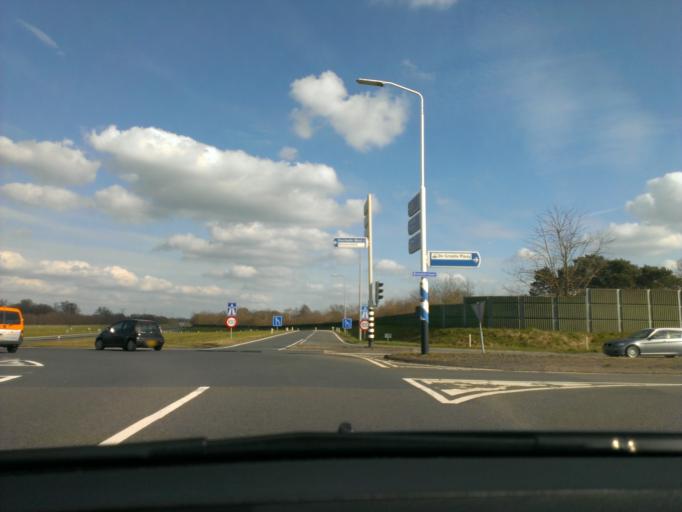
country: NL
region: Overijssel
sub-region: Gemeente Hengelo
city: Hengelo
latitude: 52.2062
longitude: 6.8227
